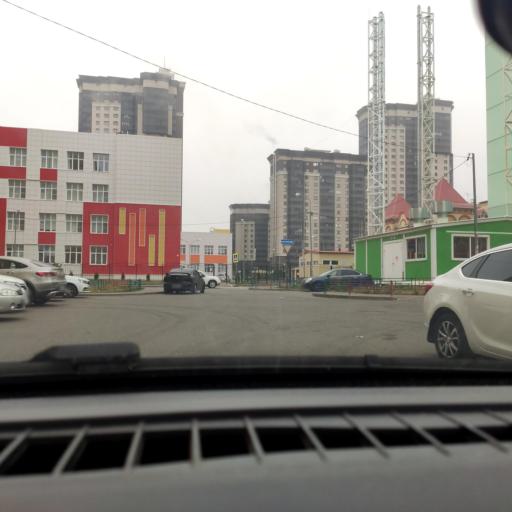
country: RU
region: Voronezj
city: Podgornoye
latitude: 51.7158
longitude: 39.1855
